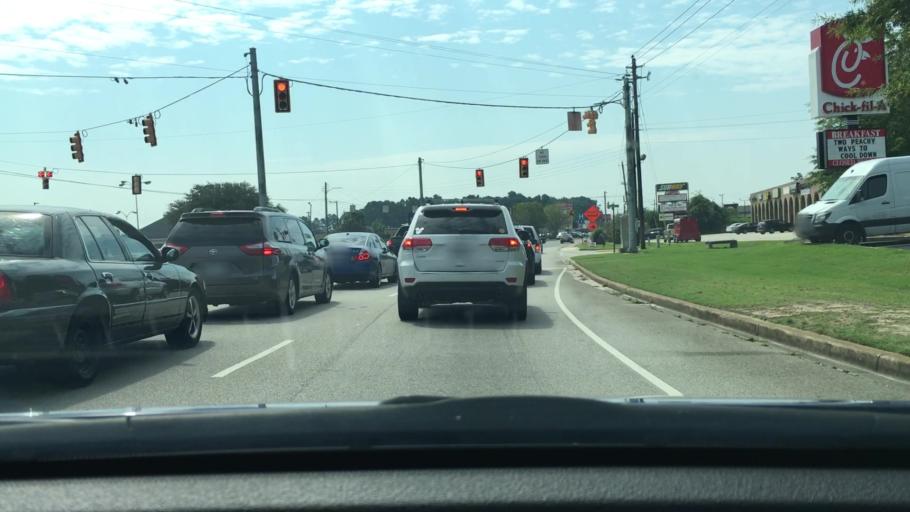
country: US
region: South Carolina
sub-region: Sumter County
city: Sumter
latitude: 33.9552
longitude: -80.3804
